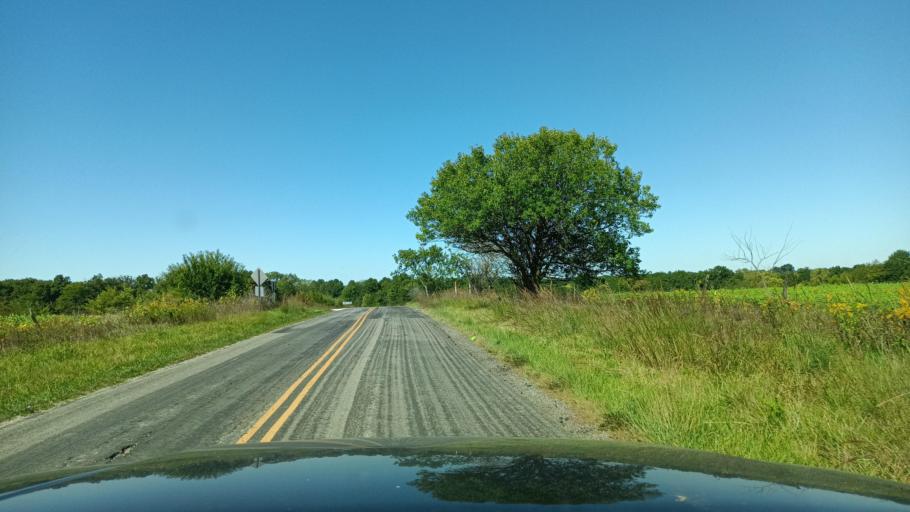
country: US
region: Missouri
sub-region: Scotland County
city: Memphis
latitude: 40.3535
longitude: -92.2753
